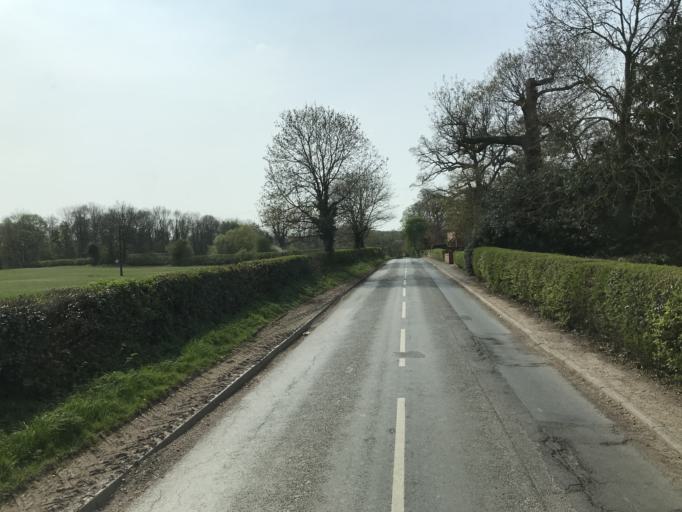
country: GB
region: England
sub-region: Cheshire West and Chester
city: Aldford
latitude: 53.1306
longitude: -2.8616
